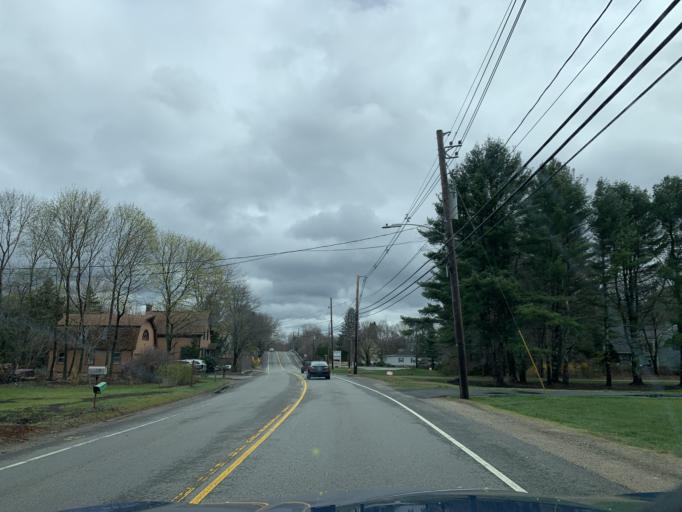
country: US
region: Massachusetts
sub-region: Bristol County
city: Mansfield Center
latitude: 42.0019
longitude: -71.2454
